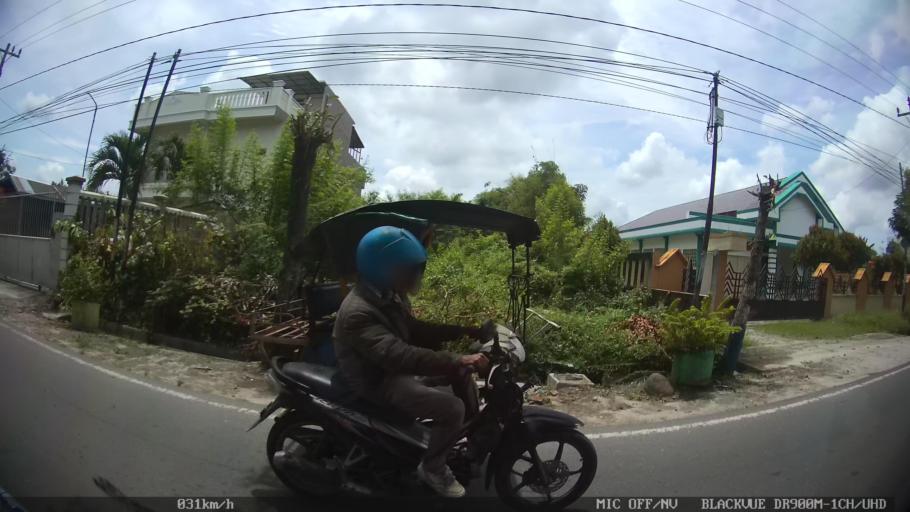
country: ID
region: North Sumatra
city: Percut
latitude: 3.5672
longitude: 98.8831
